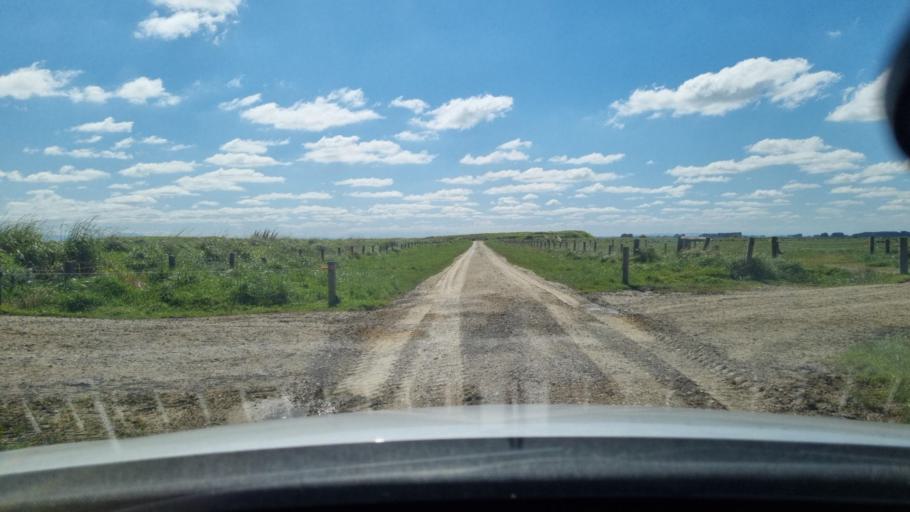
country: NZ
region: Southland
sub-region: Invercargill City
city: Invercargill
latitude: -46.3880
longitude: 168.2586
